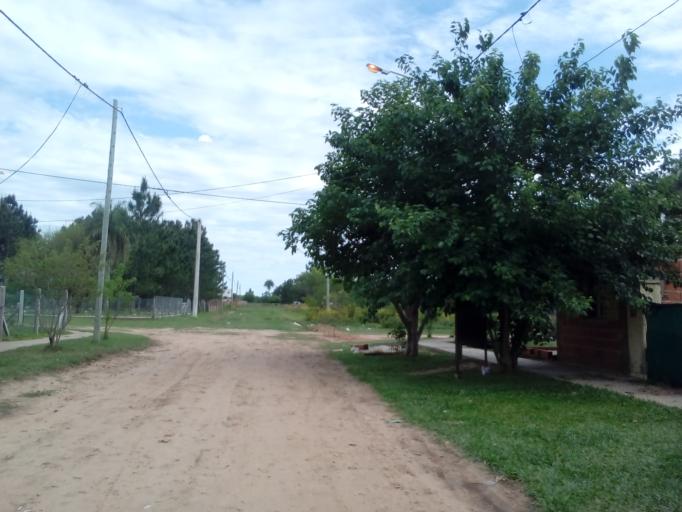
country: AR
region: Corrientes
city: San Luis del Palmar
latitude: -27.4626
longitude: -58.6530
